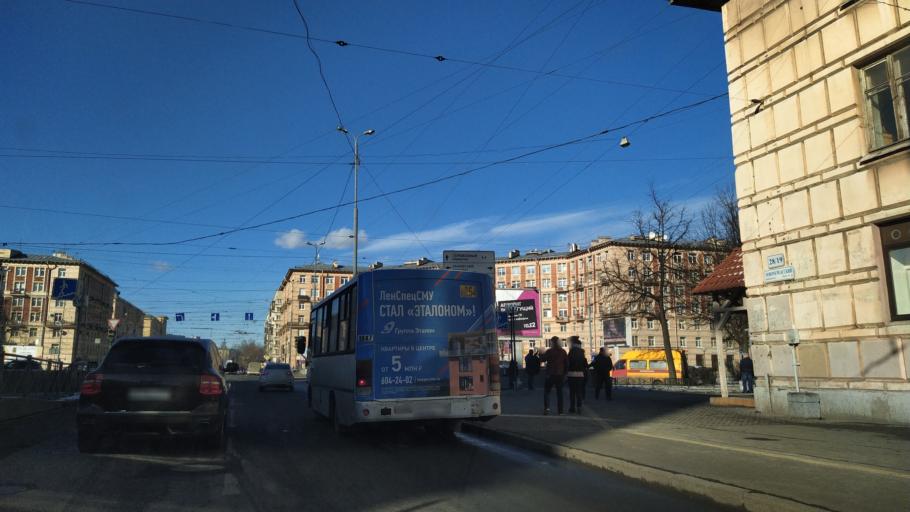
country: RU
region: St.-Petersburg
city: Centralniy
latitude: 59.9283
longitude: 30.4127
